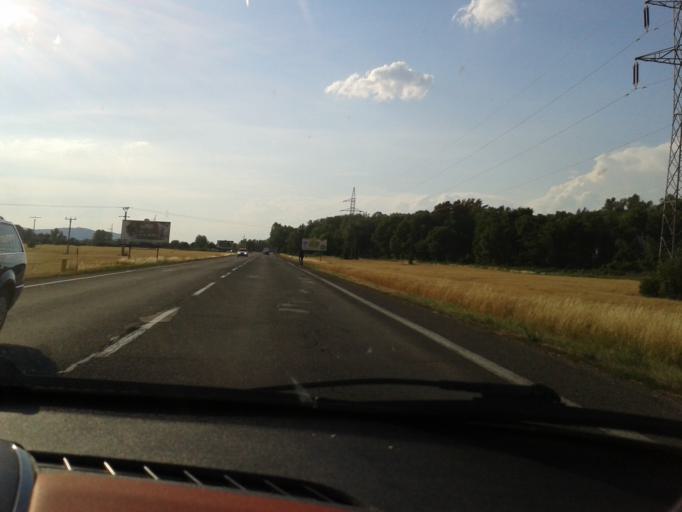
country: AT
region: Burgenland
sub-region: Politischer Bezirk Neusiedl am See
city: Deutsch Jahrndorf
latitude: 48.0765
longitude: 17.1330
